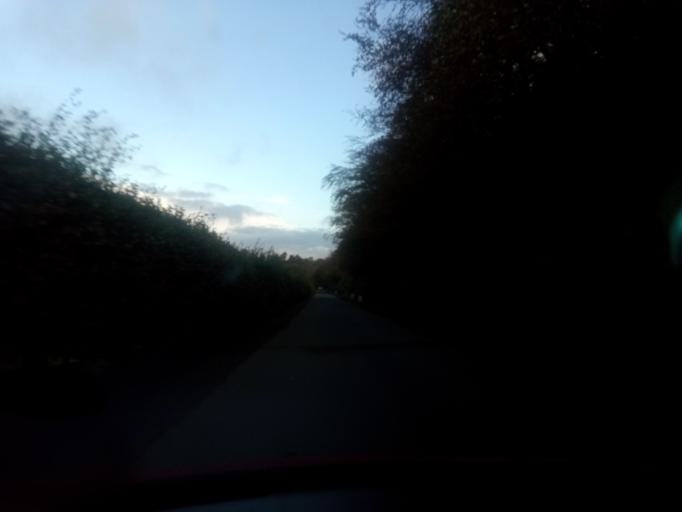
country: GB
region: Scotland
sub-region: The Scottish Borders
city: Jedburgh
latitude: 55.3850
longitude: -2.6429
